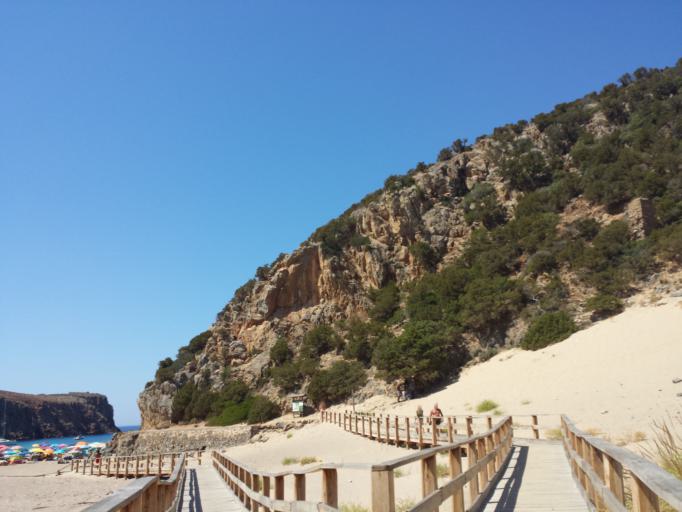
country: IT
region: Sardinia
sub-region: Provincia di Carbonia-Iglesias
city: Buggerru
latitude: 39.3732
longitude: 8.3810
